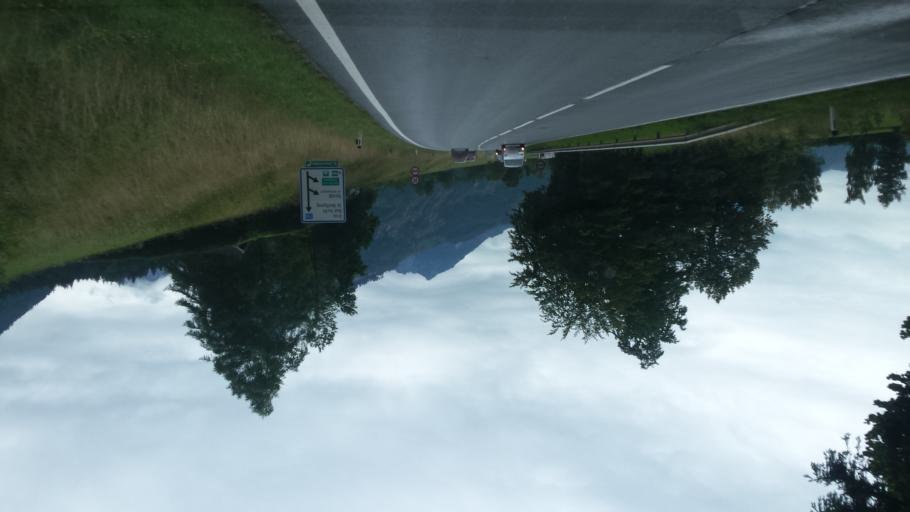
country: AT
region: Upper Austria
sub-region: Politischer Bezirk Gmunden
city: Sankt Wolfgang im Salzkammergut
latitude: 47.7187
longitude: 13.4348
